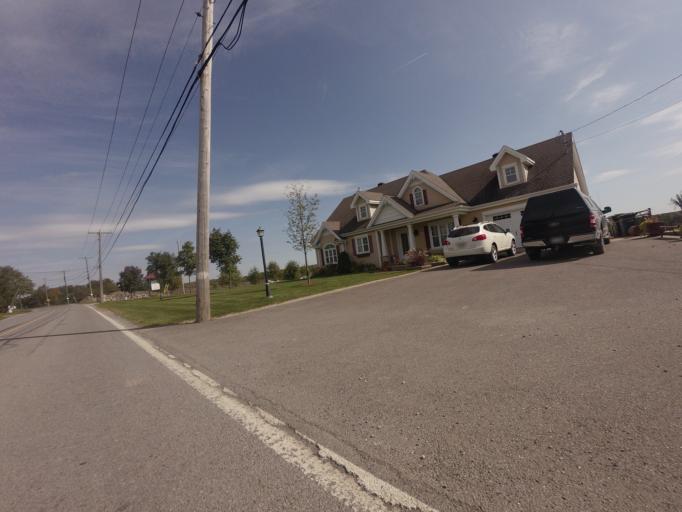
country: CA
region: Quebec
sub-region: Laurentides
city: Saint-Eustache
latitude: 45.6148
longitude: -73.9064
